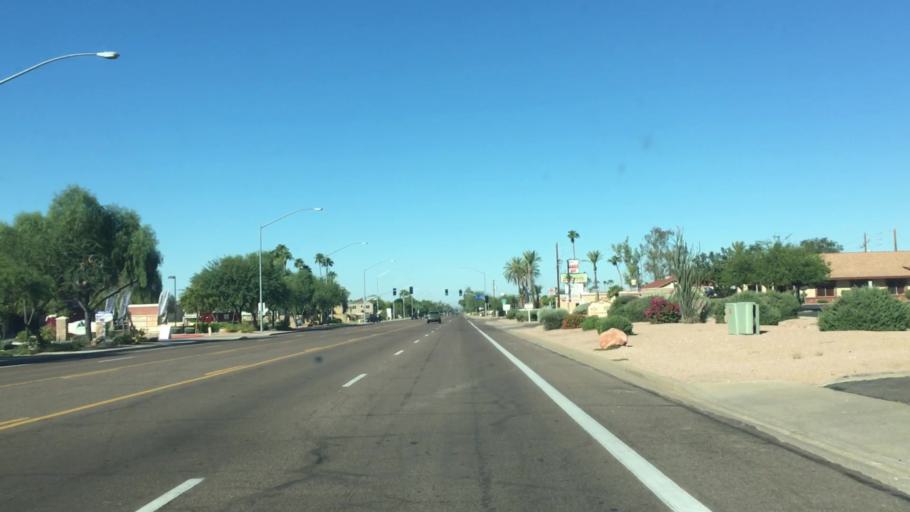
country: US
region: Arizona
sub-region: Maricopa County
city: Mesa
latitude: 33.4519
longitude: -111.7081
